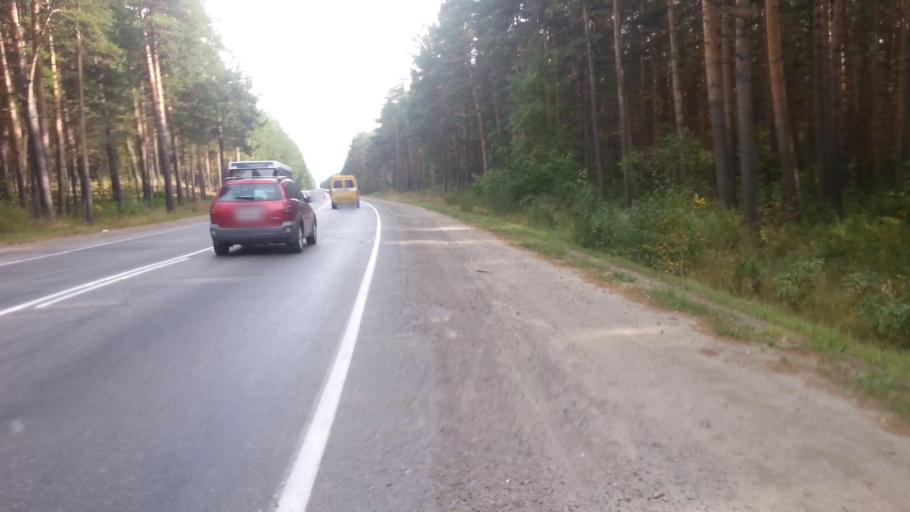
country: RU
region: Altai Krai
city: Yuzhnyy
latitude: 53.2979
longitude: 83.7031
